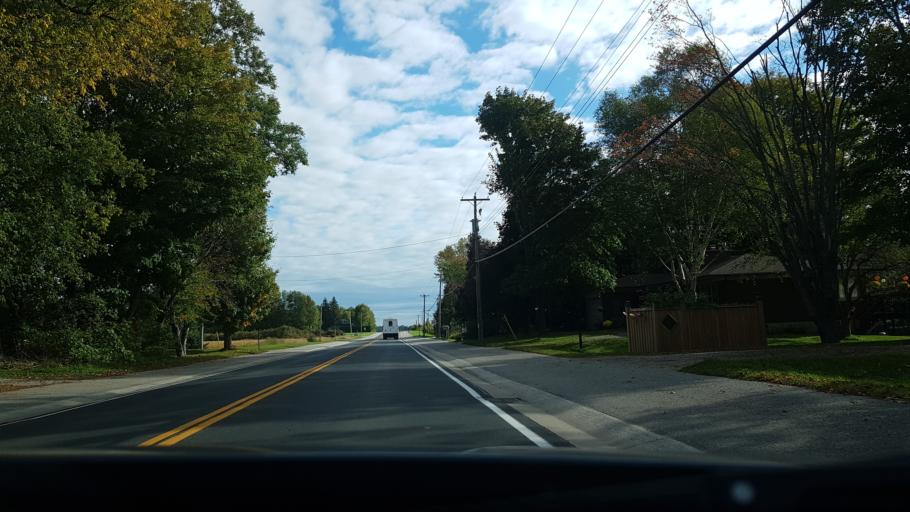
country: CA
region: Ontario
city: Orillia
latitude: 44.5960
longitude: -79.5701
